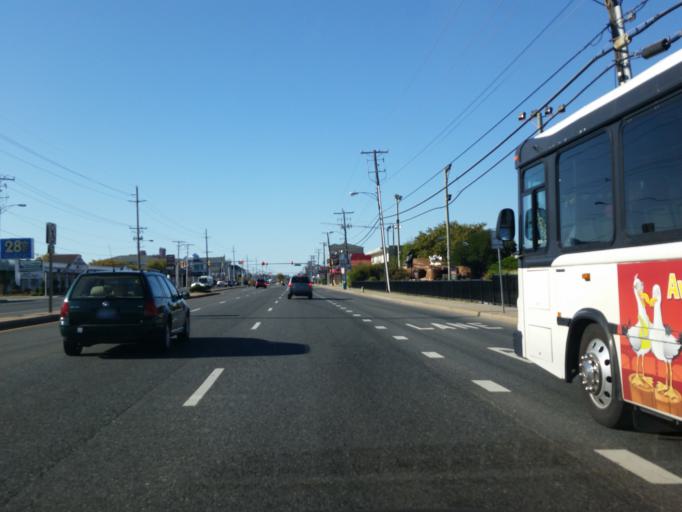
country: US
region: Maryland
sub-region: Worcester County
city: Ocean City
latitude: 38.3588
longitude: -75.0744
